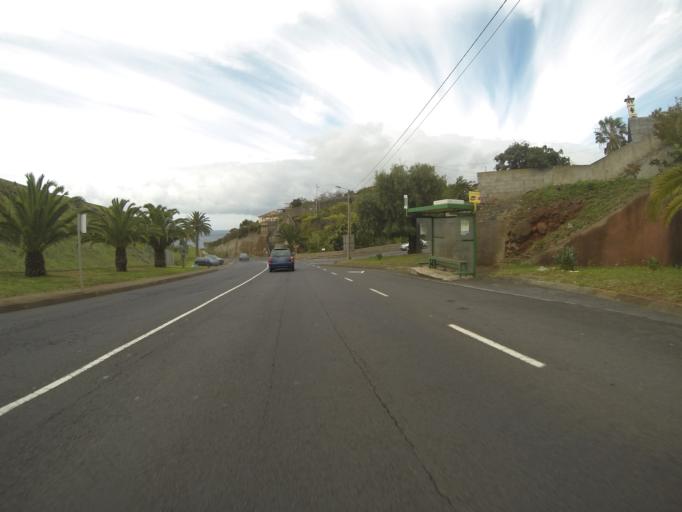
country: PT
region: Madeira
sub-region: Santa Cruz
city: Santa Cruz
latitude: 32.6905
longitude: -16.7851
